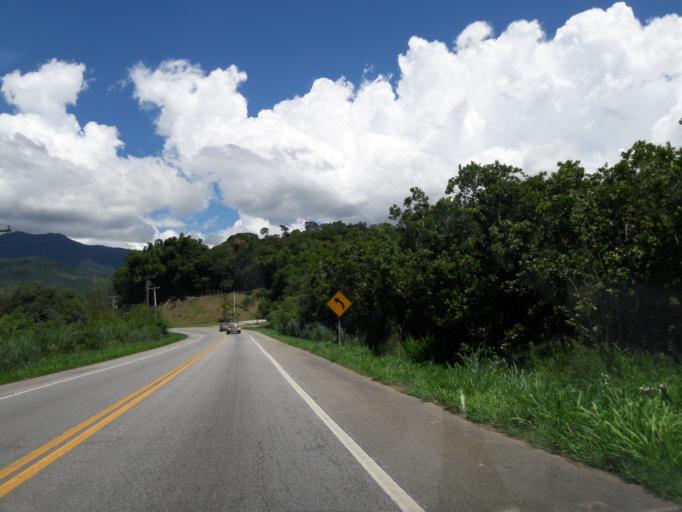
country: BR
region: Parana
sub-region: Antonina
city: Antonina
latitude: -25.5405
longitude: -48.7943
